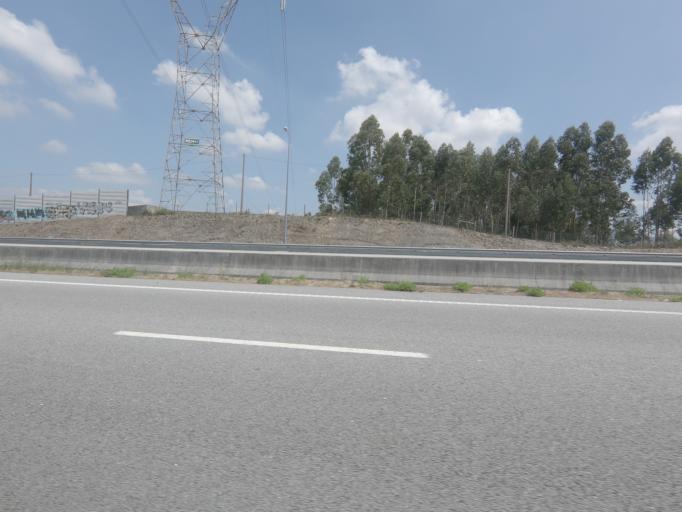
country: PT
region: Porto
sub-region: Valongo
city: Campo
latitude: 41.1805
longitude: -8.4456
